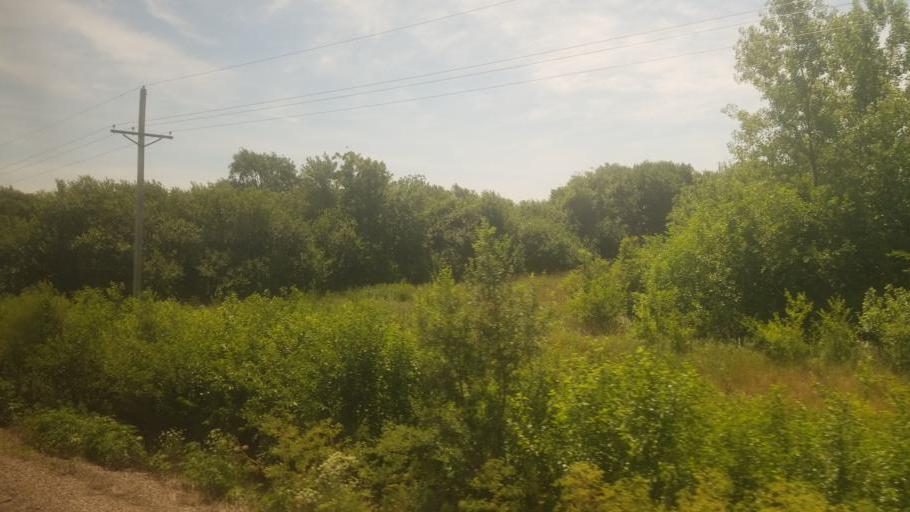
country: US
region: Missouri
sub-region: Carroll County
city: Carrollton
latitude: 39.3009
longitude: -93.6897
